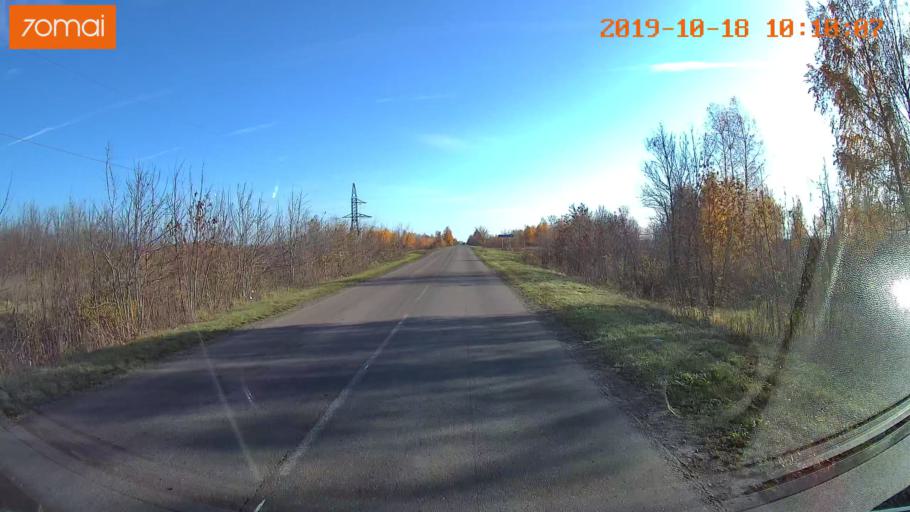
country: RU
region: Tula
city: Kurkino
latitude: 53.3783
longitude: 38.4701
